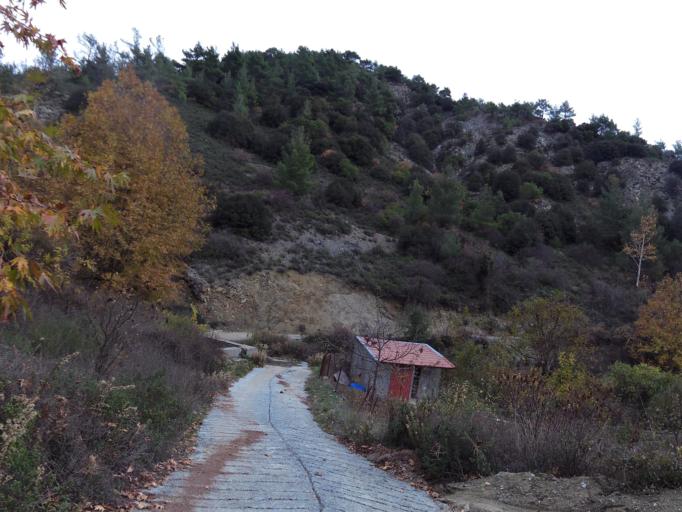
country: CY
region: Limassol
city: Kyperounta
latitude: 34.9260
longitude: 32.9447
